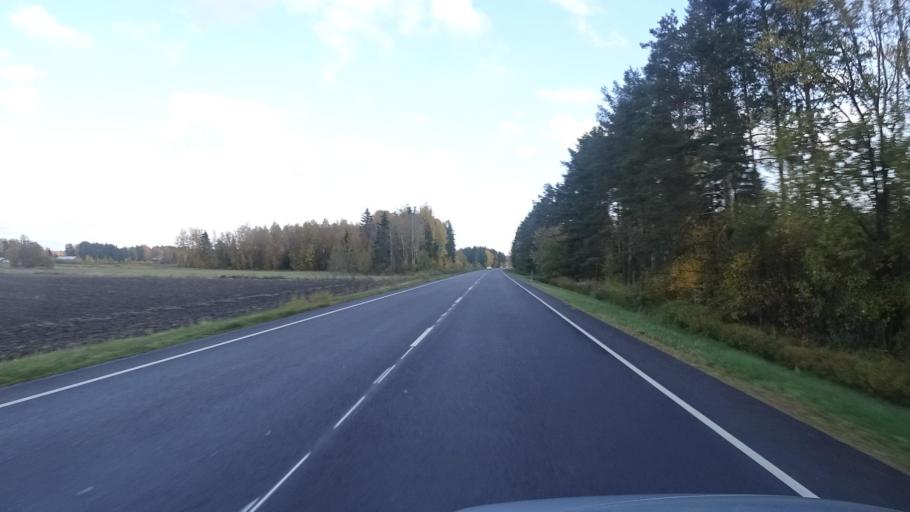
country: FI
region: Satakunta
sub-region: Rauma
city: Koeylioe
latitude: 61.0855
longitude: 22.2615
